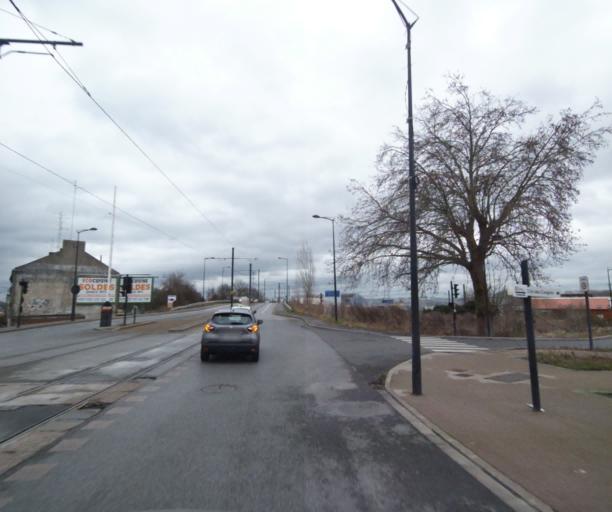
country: FR
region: Nord-Pas-de-Calais
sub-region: Departement du Nord
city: Anzin
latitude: 50.3802
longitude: 3.5209
